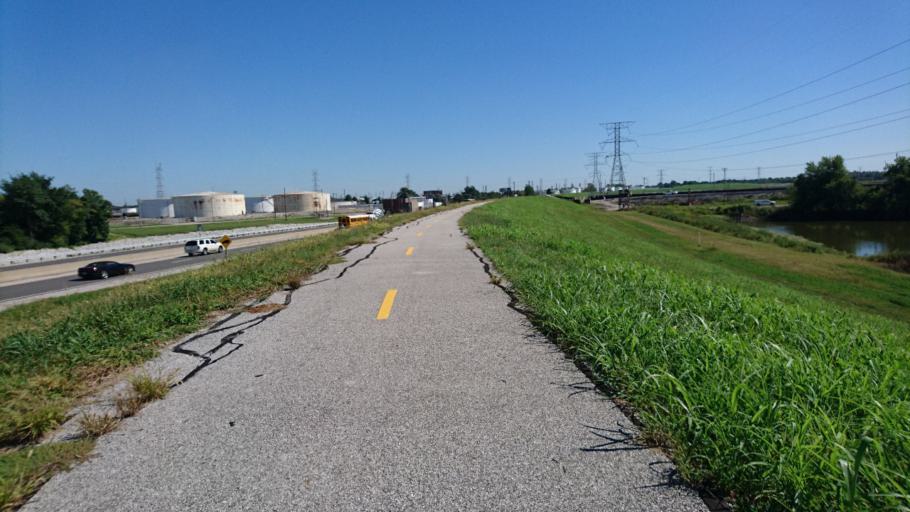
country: US
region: Illinois
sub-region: Madison County
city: Wood River
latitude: 38.8543
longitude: -90.1058
